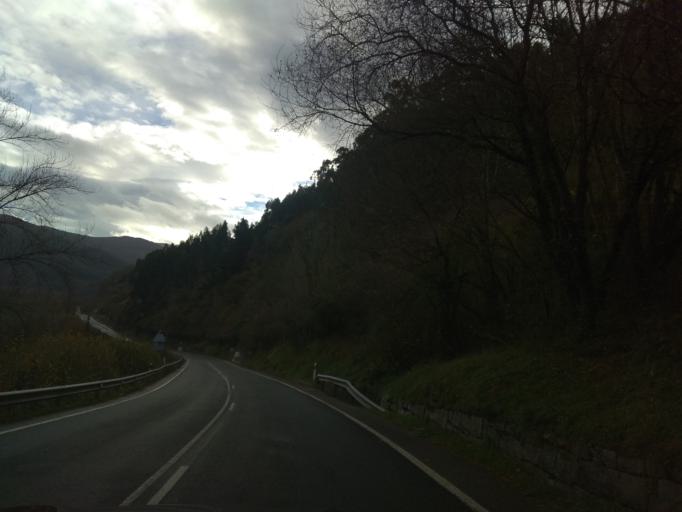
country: ES
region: Cantabria
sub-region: Provincia de Cantabria
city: Santiurde de Toranzo
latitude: 43.1820
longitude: -3.9101
